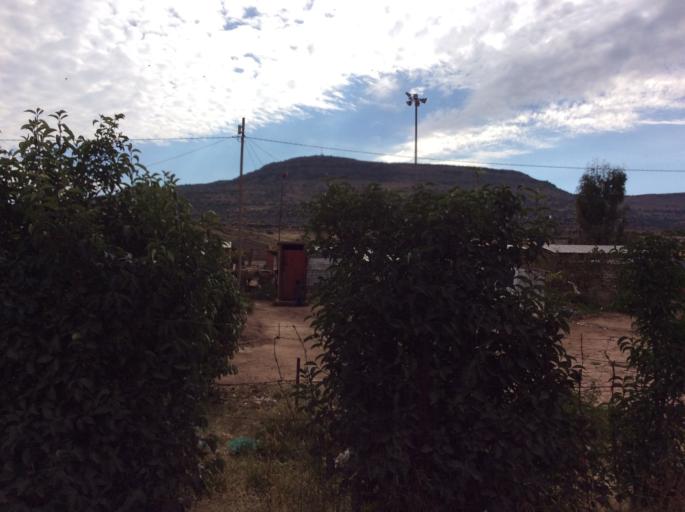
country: LS
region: Mafeteng
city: Mafeteng
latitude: -29.7185
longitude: 27.0195
